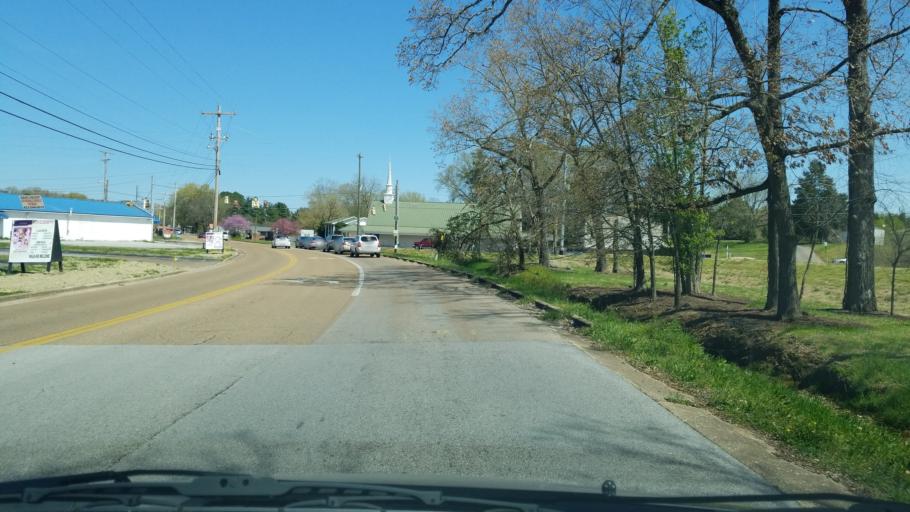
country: US
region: Tennessee
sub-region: Hamilton County
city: Middle Valley
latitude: 35.1882
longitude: -85.1904
